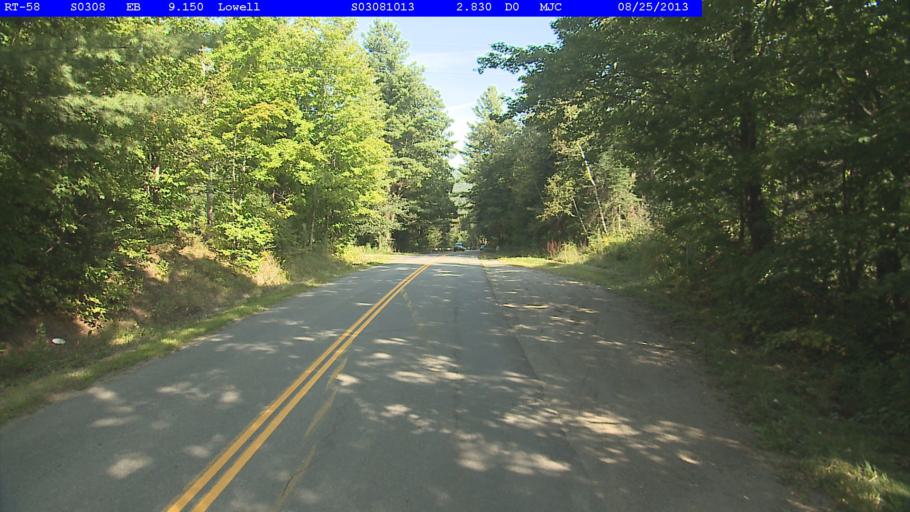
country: US
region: Vermont
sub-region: Lamoille County
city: Hyde Park
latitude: 44.8117
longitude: -72.4638
